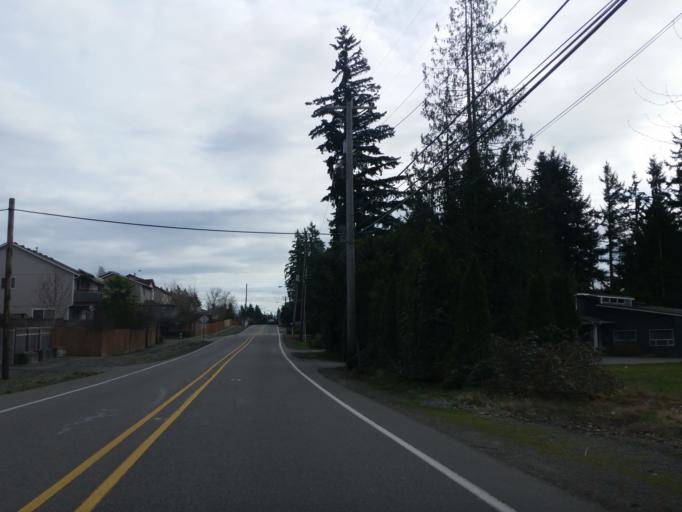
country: US
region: Washington
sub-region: Pierce County
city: South Hill
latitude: 47.1397
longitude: -122.2725
